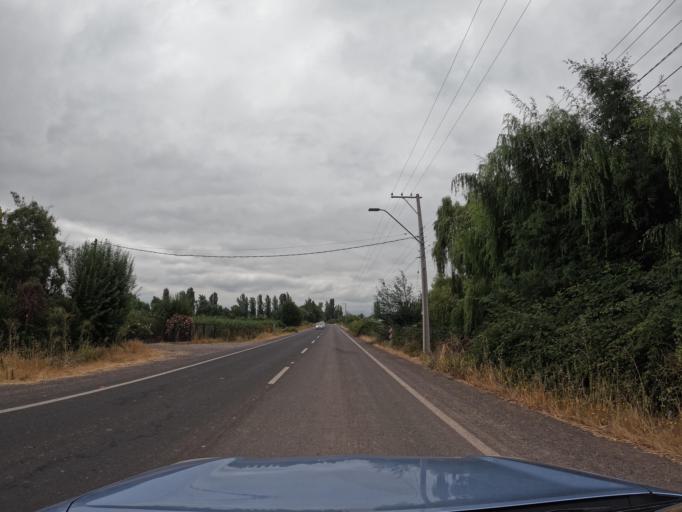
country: CL
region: O'Higgins
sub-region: Provincia de Colchagua
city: Chimbarongo
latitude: -34.7321
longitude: -71.0728
